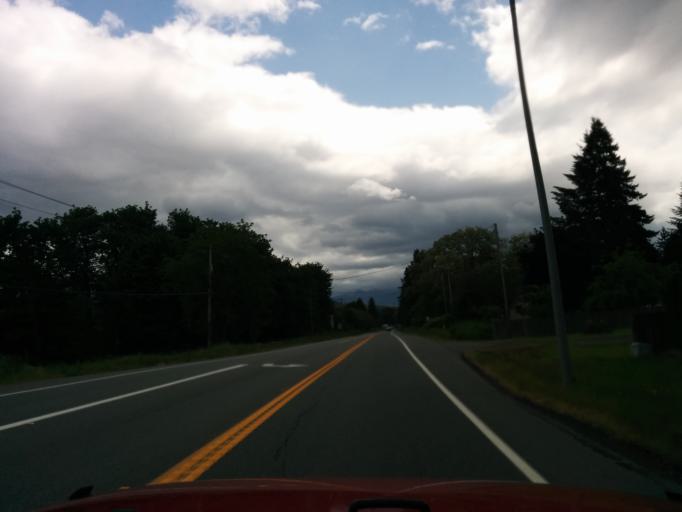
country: US
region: Washington
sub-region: King County
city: Fall City
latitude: 47.5725
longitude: -121.9048
